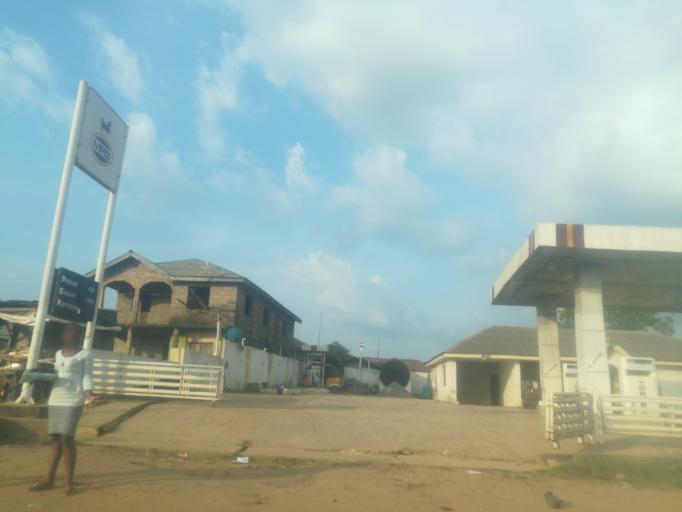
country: NG
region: Ogun
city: Abeokuta
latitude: 7.1688
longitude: 3.2972
